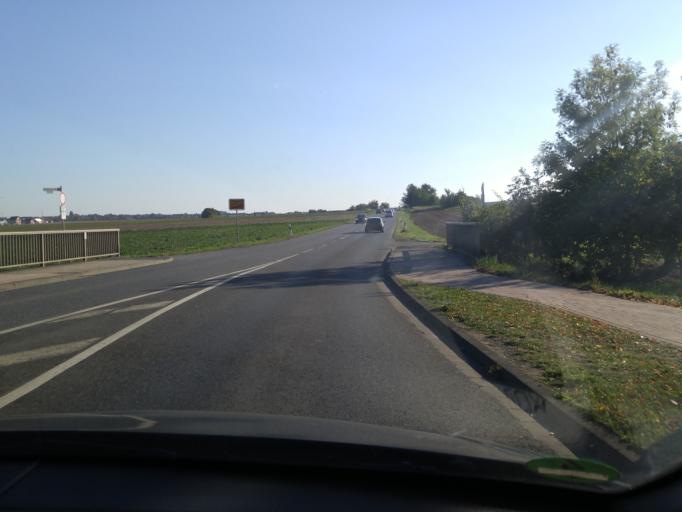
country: DE
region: Hesse
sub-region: Regierungsbezirk Darmstadt
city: Bad Nauheim
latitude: 50.3539
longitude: 8.7351
